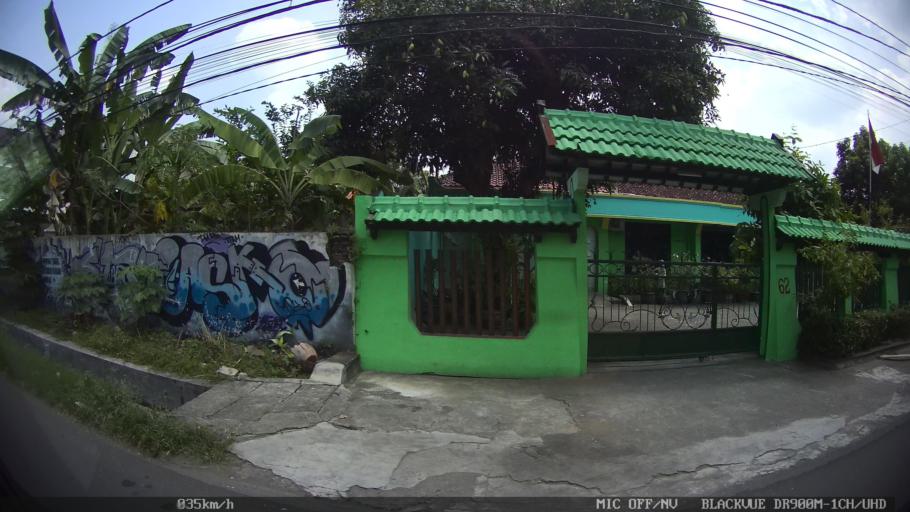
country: ID
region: Daerah Istimewa Yogyakarta
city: Yogyakarta
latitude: -7.8178
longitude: 110.3979
